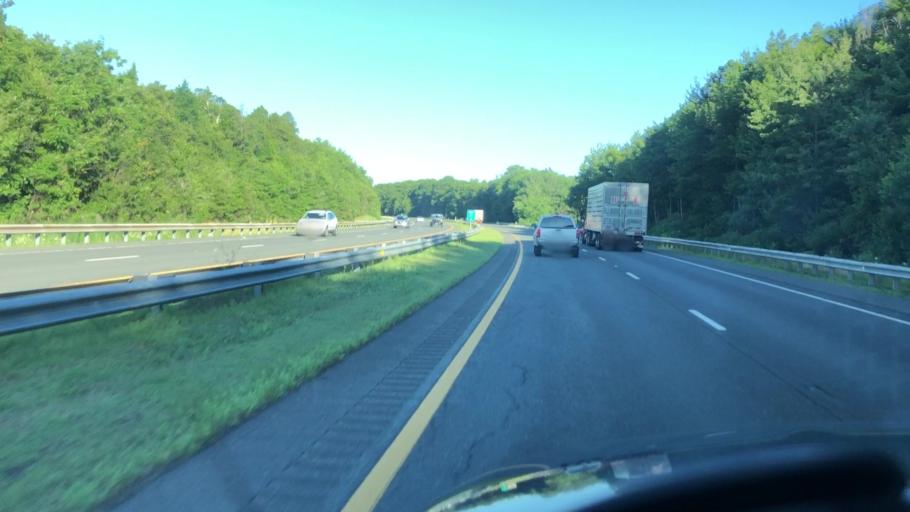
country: US
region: Massachusetts
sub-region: Berkshire County
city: Otis
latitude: 42.2380
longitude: -72.9967
